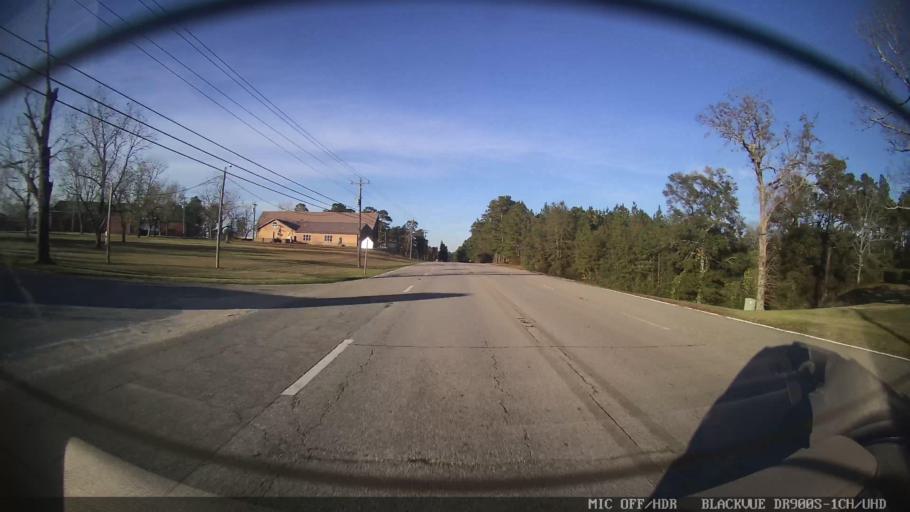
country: US
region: Mississippi
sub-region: Lamar County
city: Purvis
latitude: 31.0997
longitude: -89.4134
